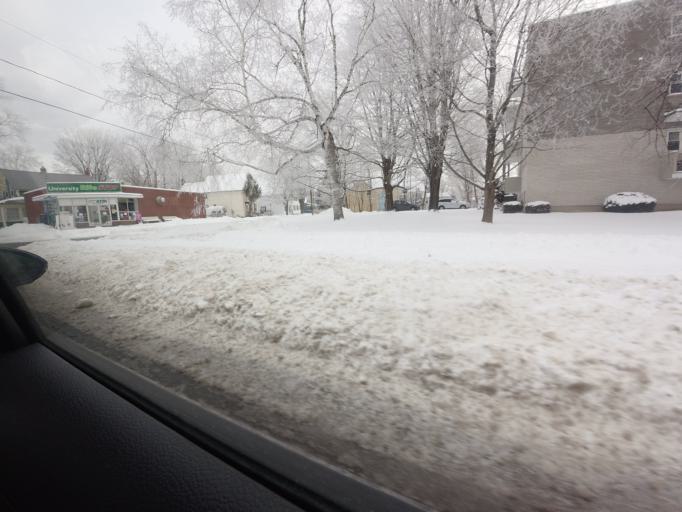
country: CA
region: New Brunswick
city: Fredericton
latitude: 45.9537
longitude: -66.6356
